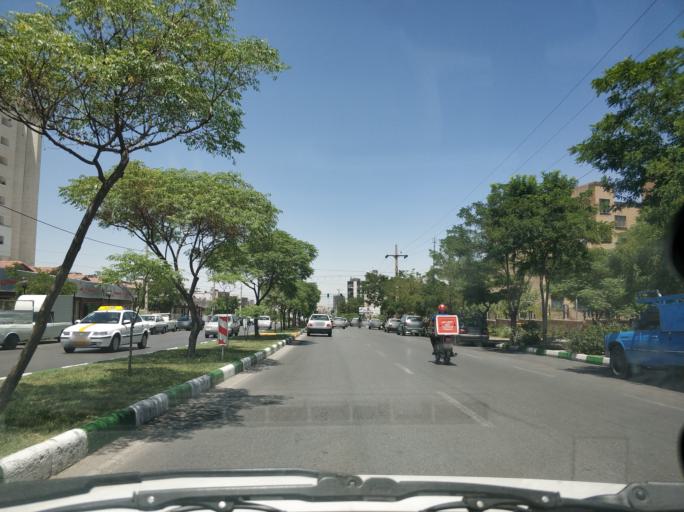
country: IR
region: Razavi Khorasan
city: Mashhad
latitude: 36.2995
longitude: 59.5098
